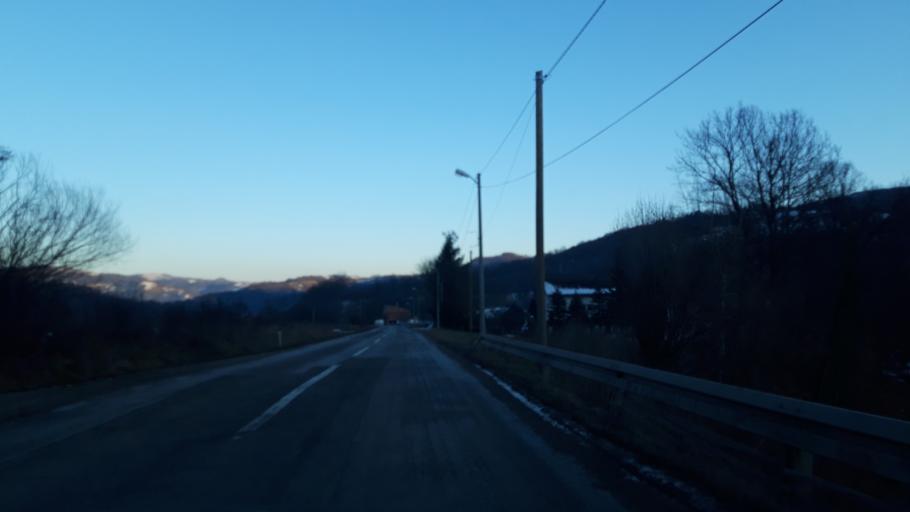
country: BA
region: Republika Srpska
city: Milici
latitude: 44.1644
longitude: 19.0448
